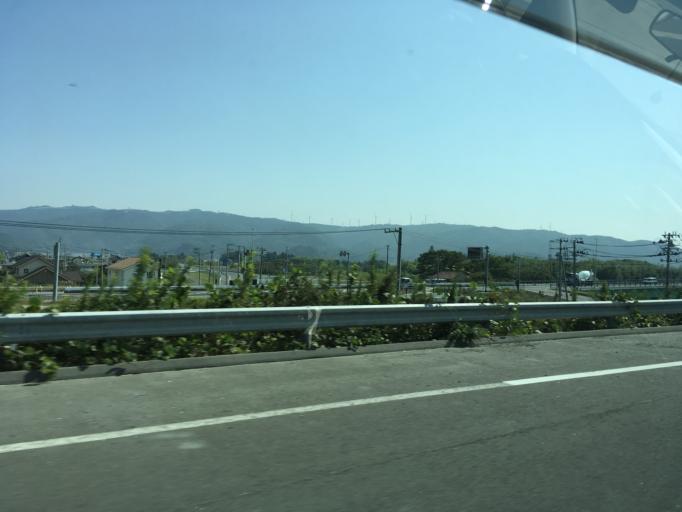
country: JP
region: Miyagi
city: Ishinomaki
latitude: 38.4956
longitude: 141.2883
